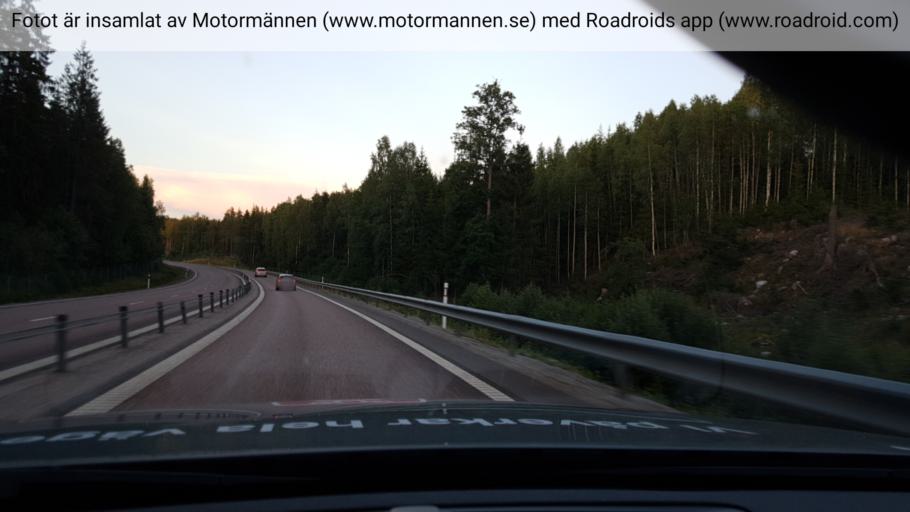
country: SE
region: Vaestmanland
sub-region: Fagersta Kommun
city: Fagersta
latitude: 59.9418
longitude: 15.8710
